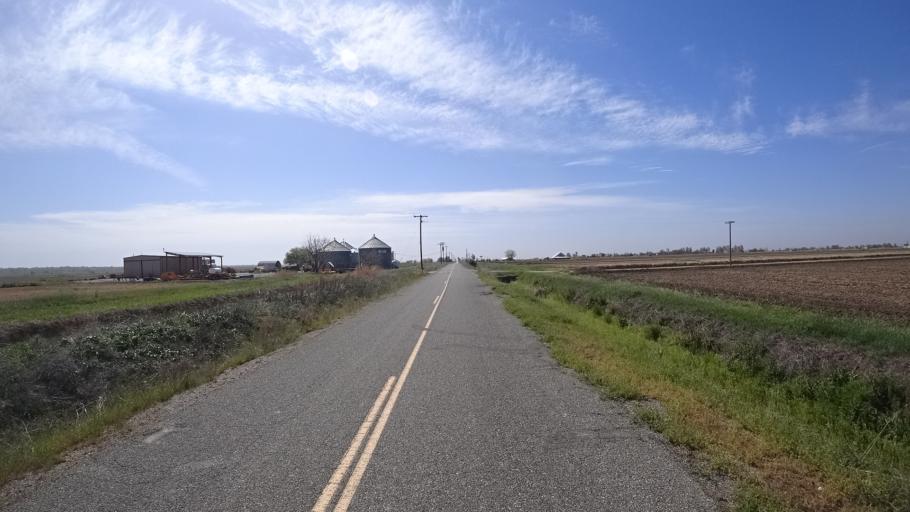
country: US
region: California
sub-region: Glenn County
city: Hamilton City
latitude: 39.5950
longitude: -122.0276
